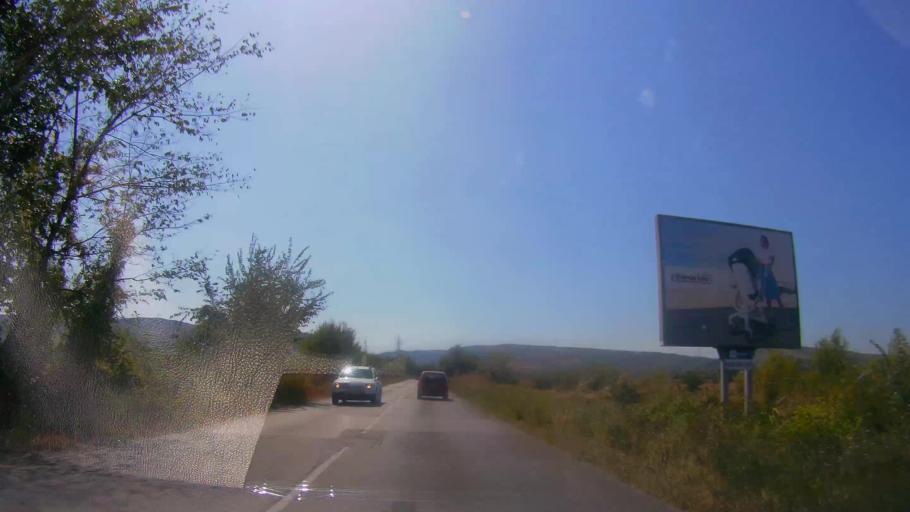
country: BG
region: Veliko Turnovo
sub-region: Obshtina Gorna Oryakhovitsa
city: Purvomaytsi
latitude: 43.1553
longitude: 25.6186
